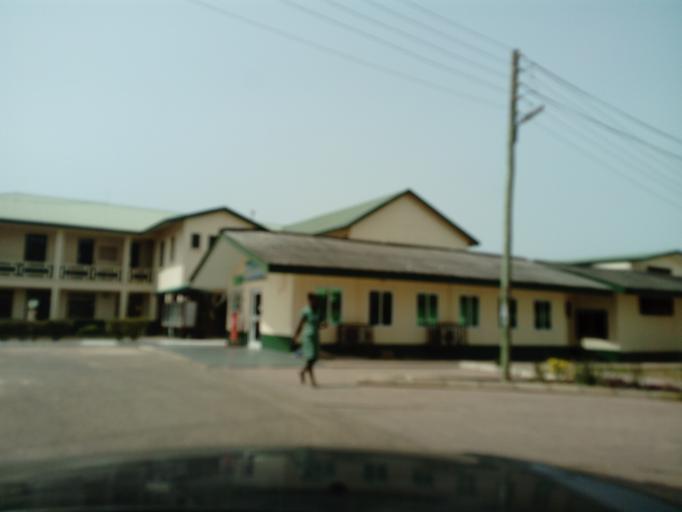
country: GH
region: Central
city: Cape Coast
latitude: 5.1046
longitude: -1.2741
